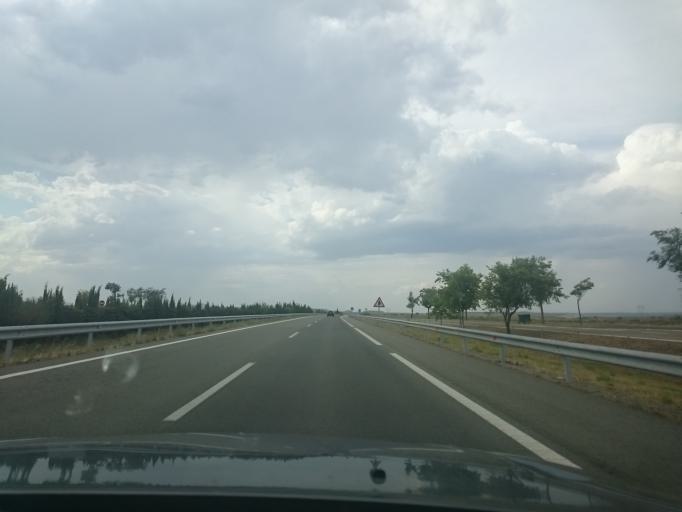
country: ES
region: Navarre
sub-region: Provincia de Navarra
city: Corella
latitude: 42.1644
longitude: -1.8258
